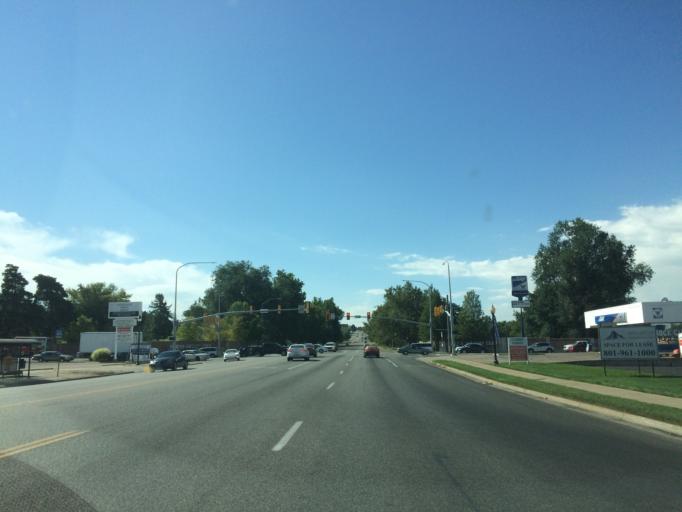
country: US
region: Utah
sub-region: Weber County
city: South Ogden
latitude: 41.1914
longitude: -111.9713
